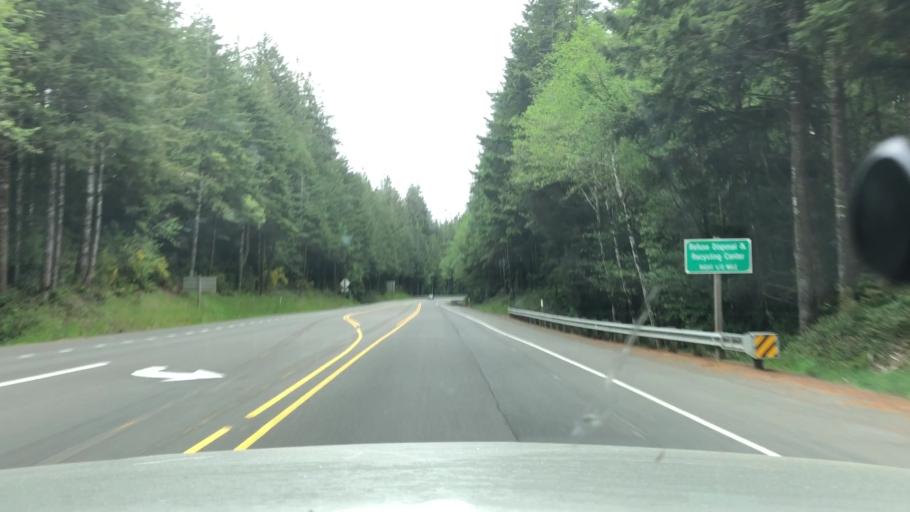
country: US
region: Oregon
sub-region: Coos County
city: Coquille
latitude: 43.2089
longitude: -124.3069
